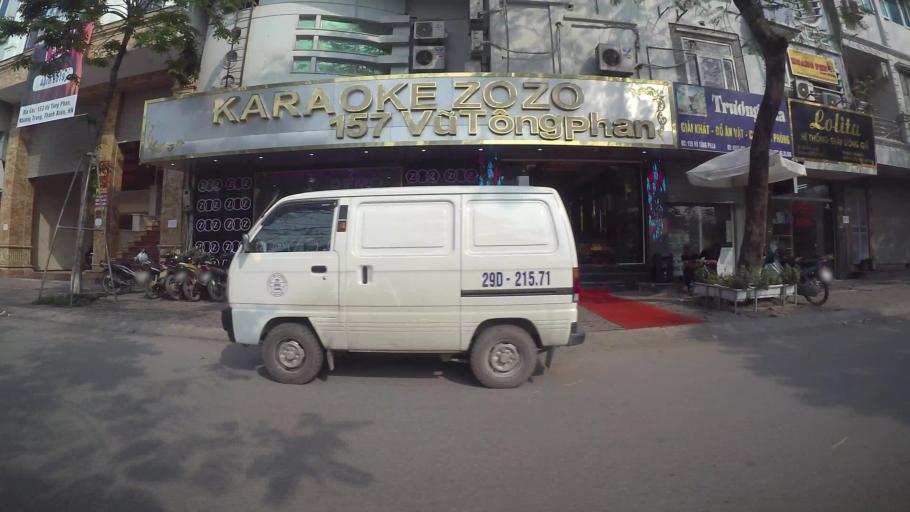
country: VN
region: Ha Noi
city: Thanh Xuan
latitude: 20.9965
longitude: 105.8161
